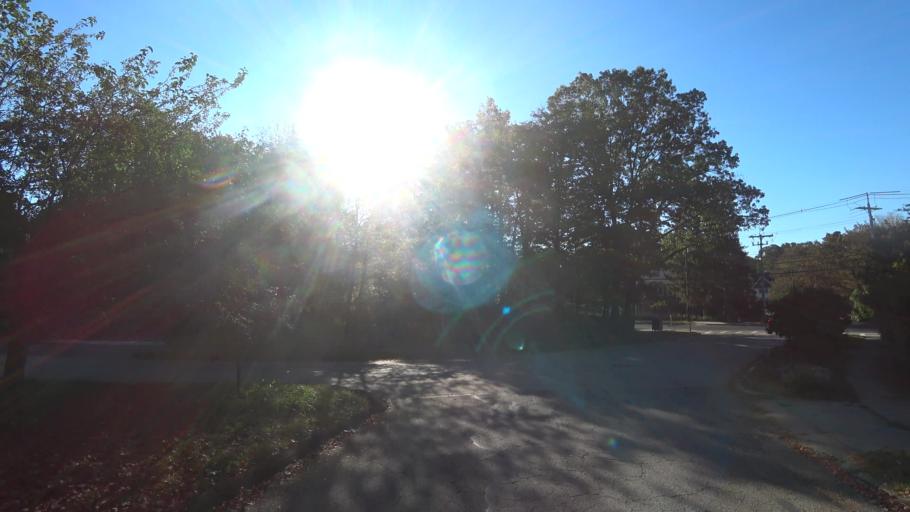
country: US
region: Massachusetts
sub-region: Middlesex County
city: Newton
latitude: 42.3354
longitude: -71.2017
